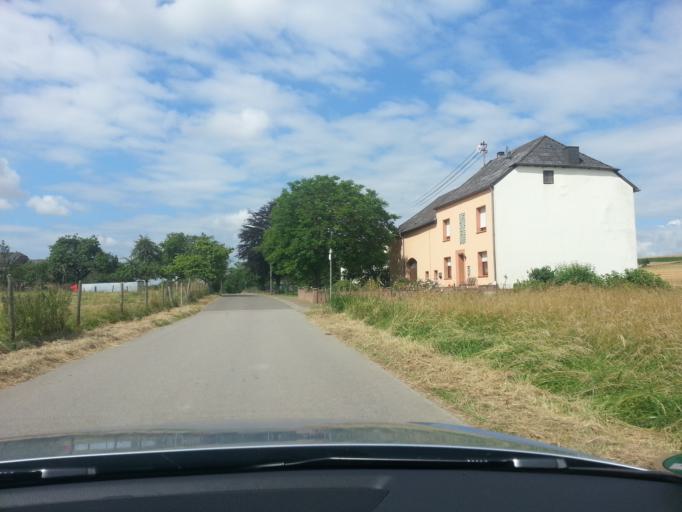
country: DE
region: Rheinland-Pfalz
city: Kirf
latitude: 49.5156
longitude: 6.4834
